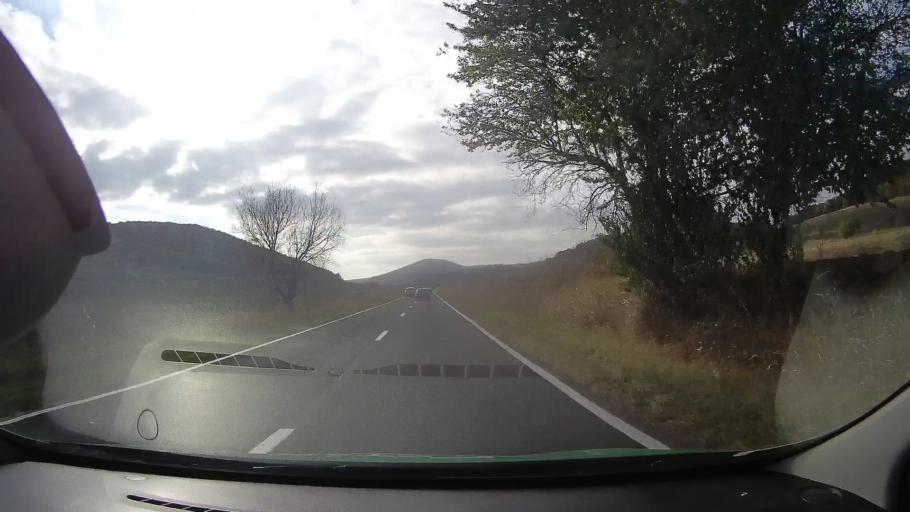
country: RO
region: Tulcea
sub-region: Comuna Ciucurova
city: Ciucurova
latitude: 44.9664
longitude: 28.5312
